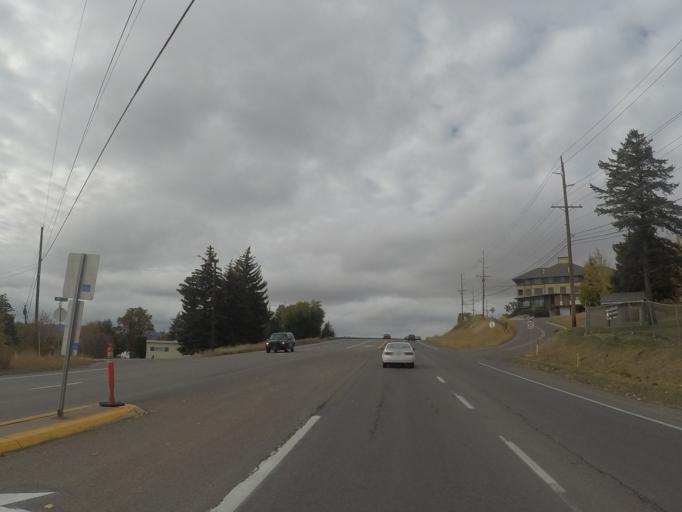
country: US
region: Montana
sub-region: Flathead County
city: Kalispell
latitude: 48.2084
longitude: -114.3232
